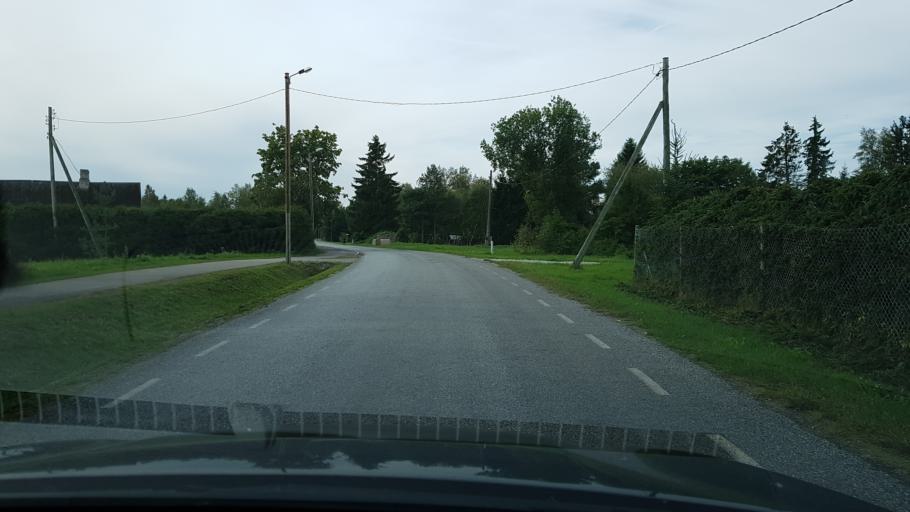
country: EE
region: Harju
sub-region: Raasiku vald
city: Raasiku
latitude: 59.4444
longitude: 25.1715
